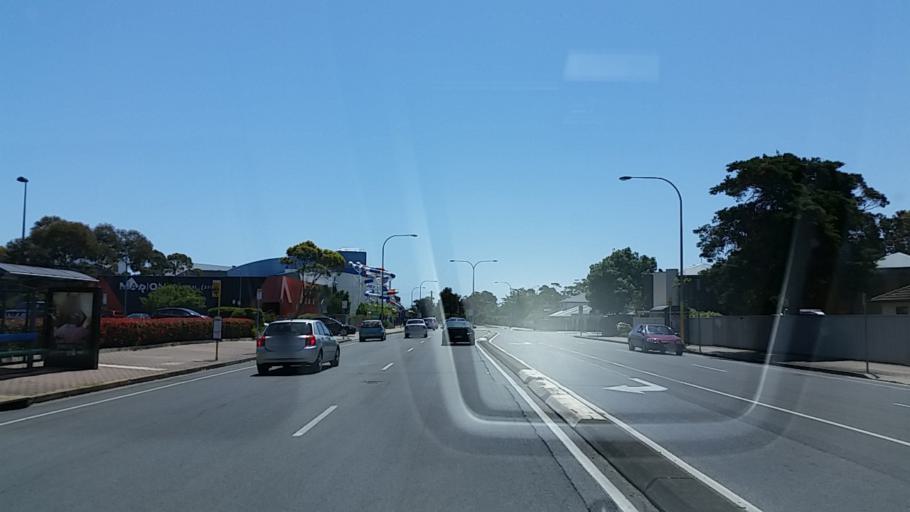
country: AU
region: South Australia
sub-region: Marion
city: Sturt
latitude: -35.0138
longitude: 138.5447
